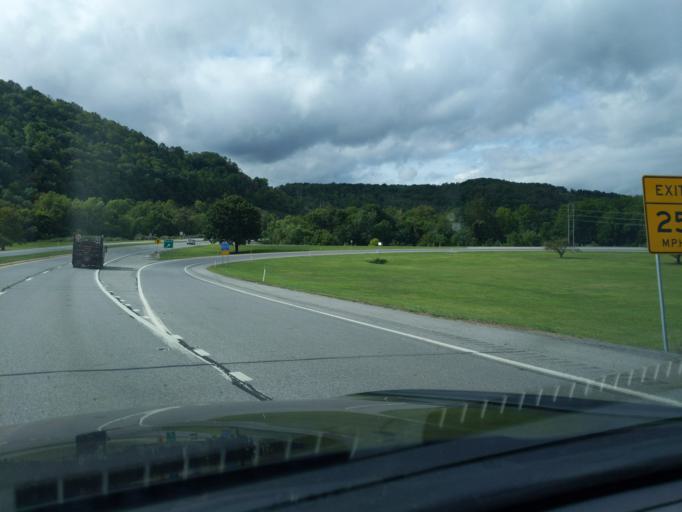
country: US
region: Pennsylvania
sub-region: Blair County
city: Hollidaysburg
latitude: 40.4251
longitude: -78.3884
